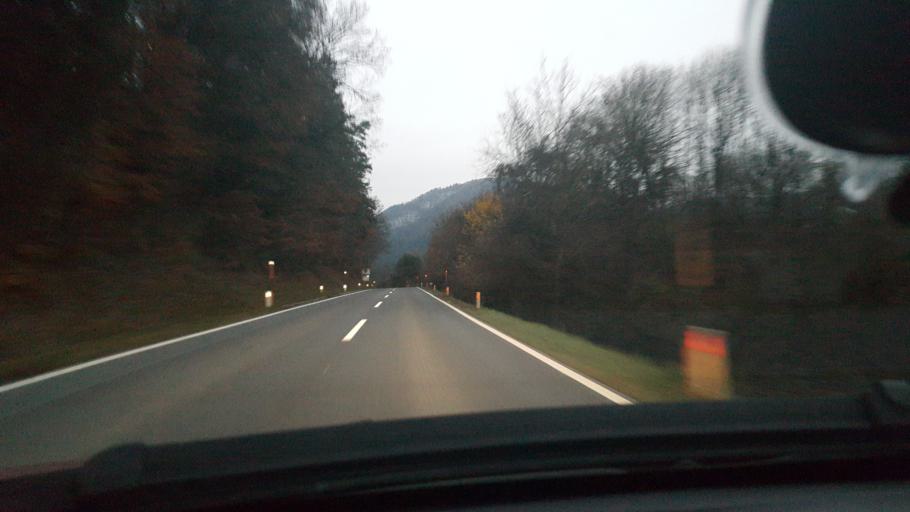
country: AT
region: Carinthia
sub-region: Politischer Bezirk Volkermarkt
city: Neuhaus
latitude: 46.6552
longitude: 14.8881
